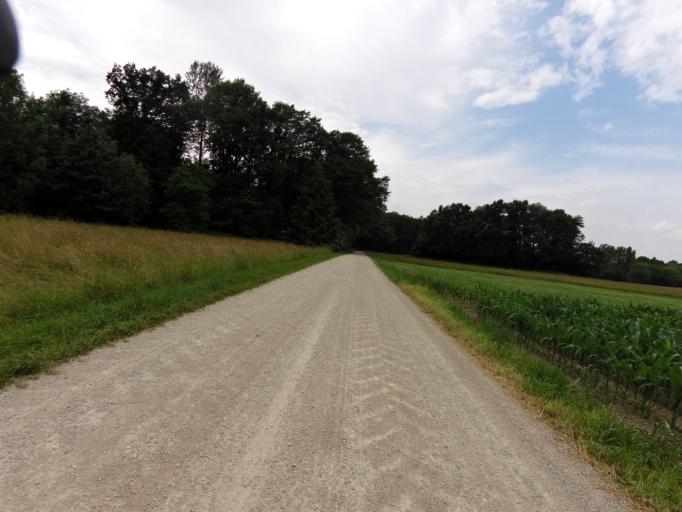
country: DE
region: Bavaria
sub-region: Upper Bavaria
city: Langenbach
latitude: 48.4559
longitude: 11.8787
